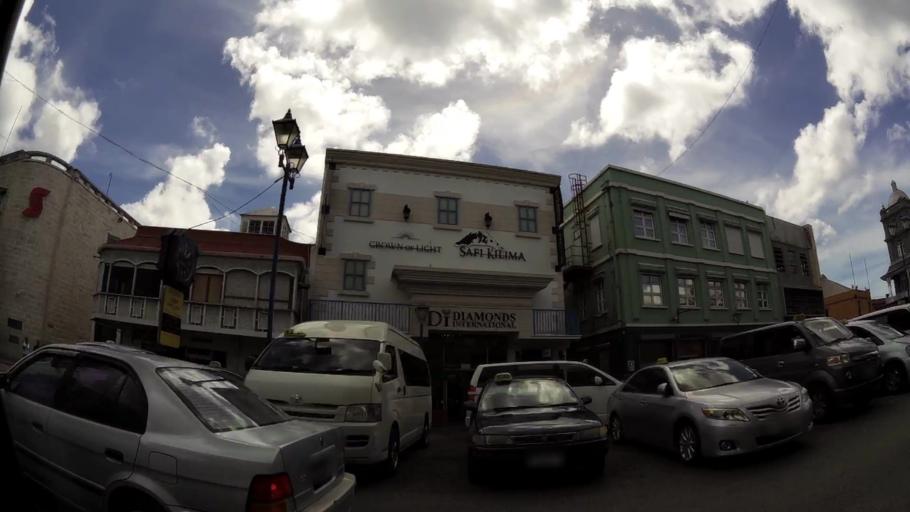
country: BB
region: Saint Michael
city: Bridgetown
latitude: 13.0976
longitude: -59.6169
